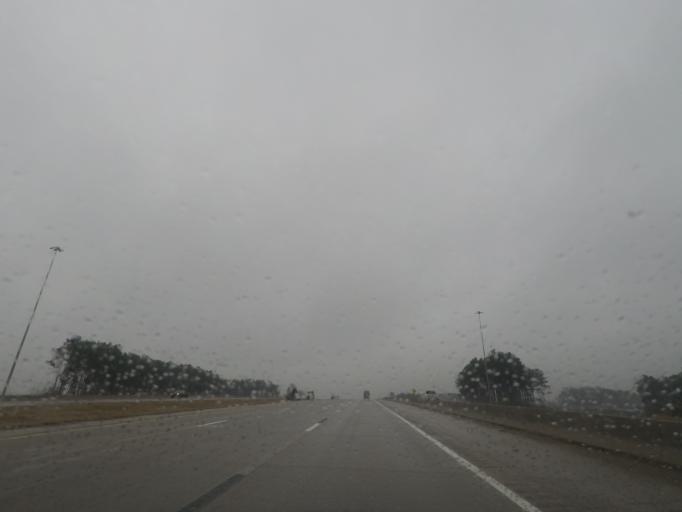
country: US
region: North Carolina
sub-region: Wake County
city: Green Level
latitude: 35.7506
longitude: -78.8921
